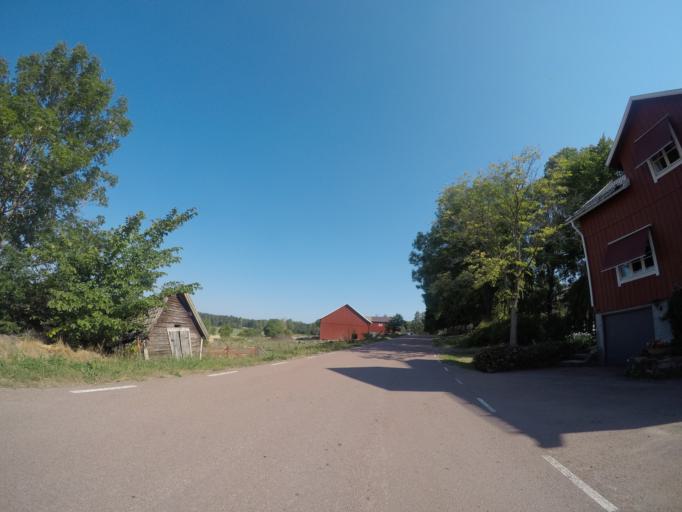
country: AX
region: Alands landsbygd
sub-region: Jomala
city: Jomala
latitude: 60.2071
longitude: 19.9733
